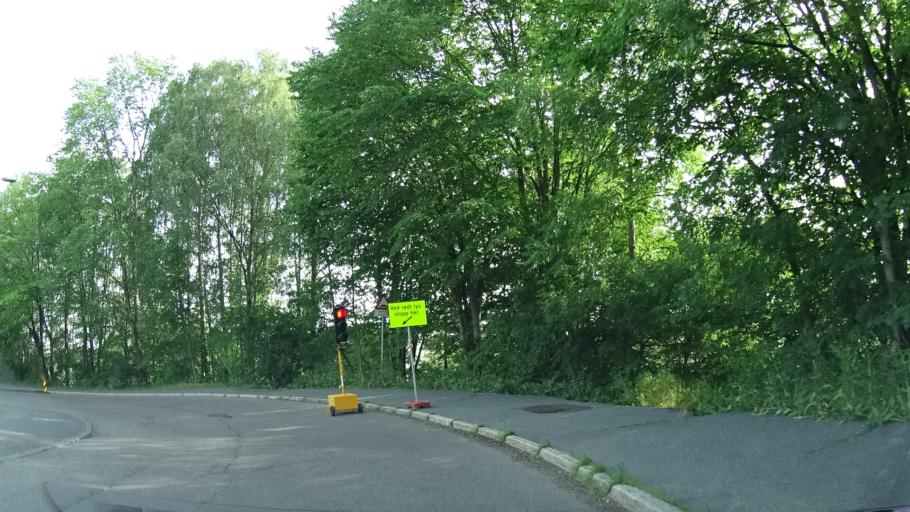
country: NO
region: Oslo
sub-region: Oslo
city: Sjolyststranda
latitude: 59.9561
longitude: 10.6551
